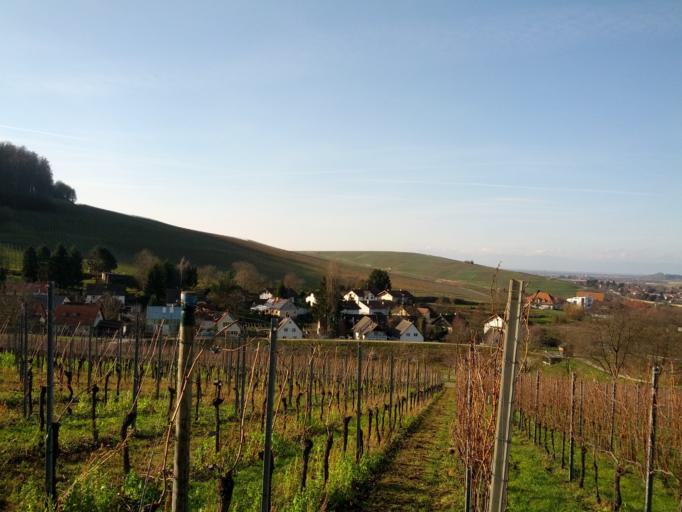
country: DE
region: Baden-Wuerttemberg
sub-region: Freiburg Region
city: Ebringen
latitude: 47.9537
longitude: 7.7774
